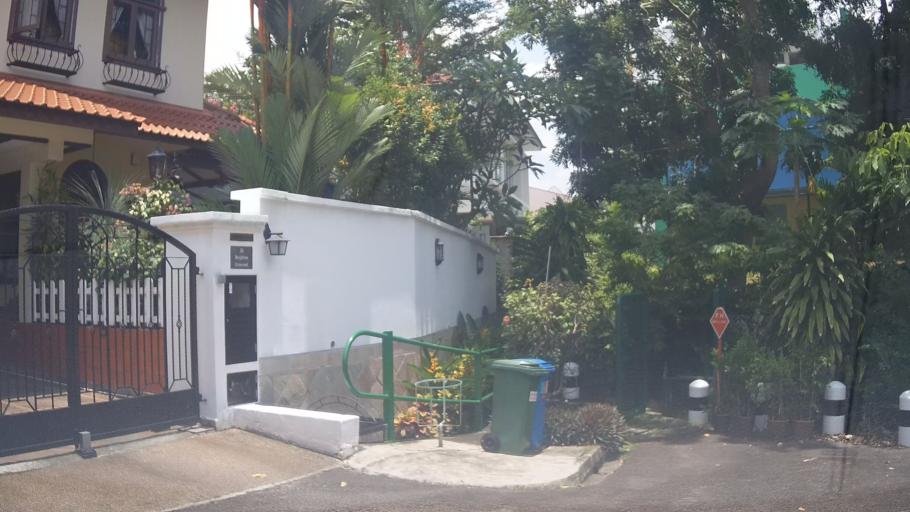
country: SG
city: Singapore
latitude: 1.3609
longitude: 103.8697
